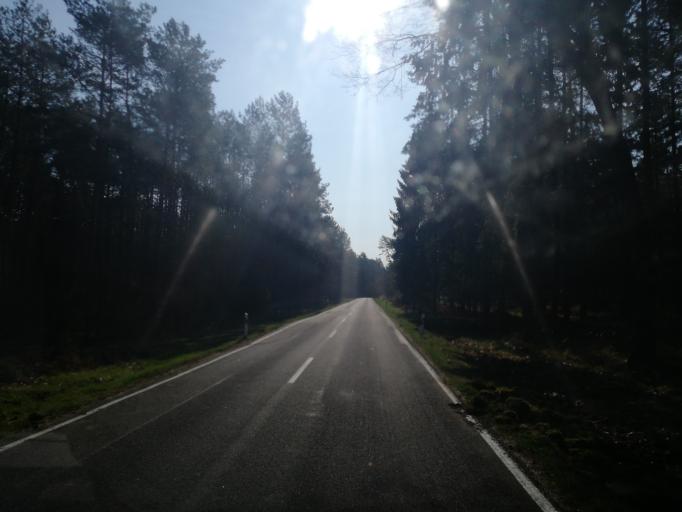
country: DE
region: Brandenburg
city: Sonnewalde
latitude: 51.7643
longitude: 13.6577
